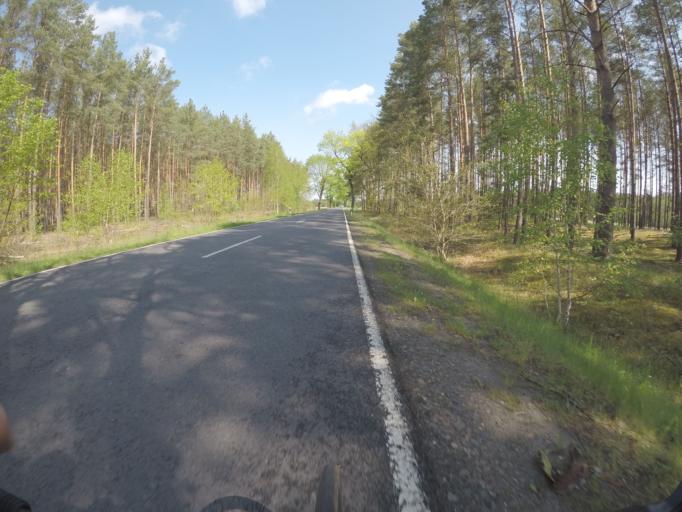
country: DE
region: Brandenburg
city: Marienwerder
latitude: 52.8143
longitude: 13.5562
